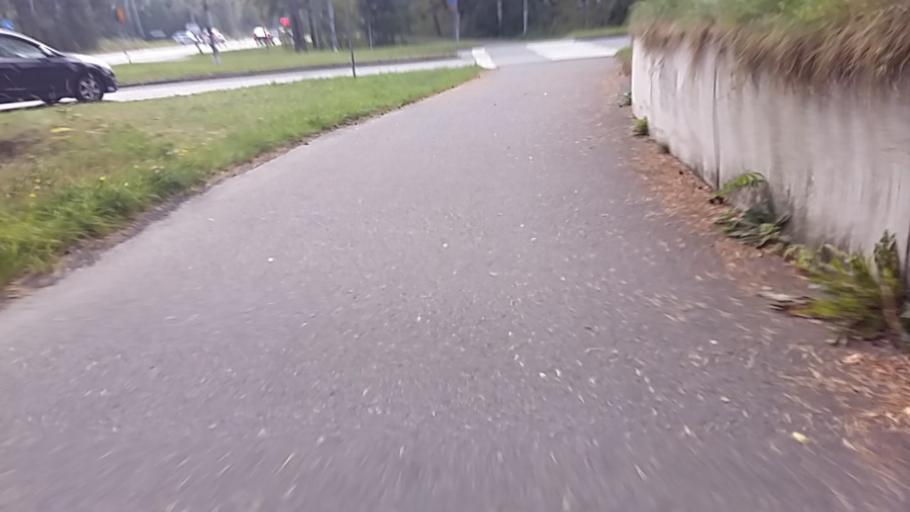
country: SE
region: Joenkoeping
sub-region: Jonkopings Kommun
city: Odensjo
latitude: 57.7429
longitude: 14.1567
